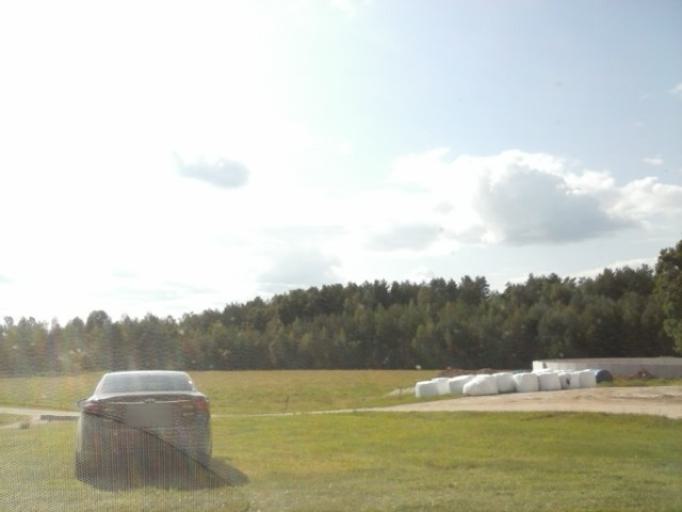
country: EE
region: Vorumaa
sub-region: Voru linn
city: Voru
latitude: 57.8449
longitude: 27.1912
